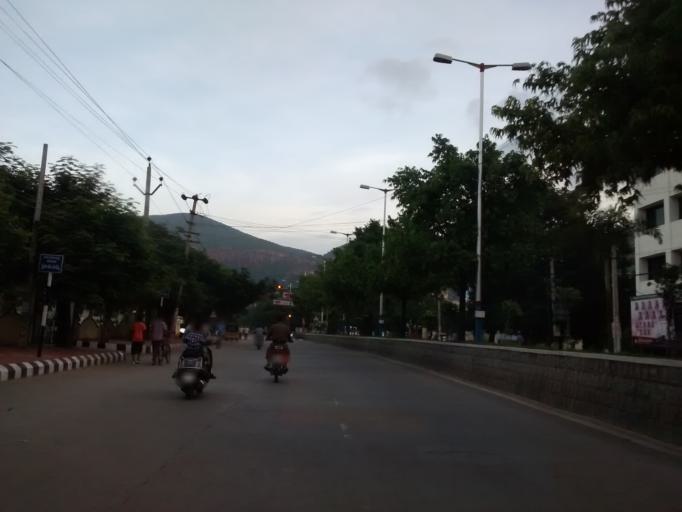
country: IN
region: Andhra Pradesh
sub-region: Chittoor
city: Akkarampalle
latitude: 13.6468
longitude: 79.4267
